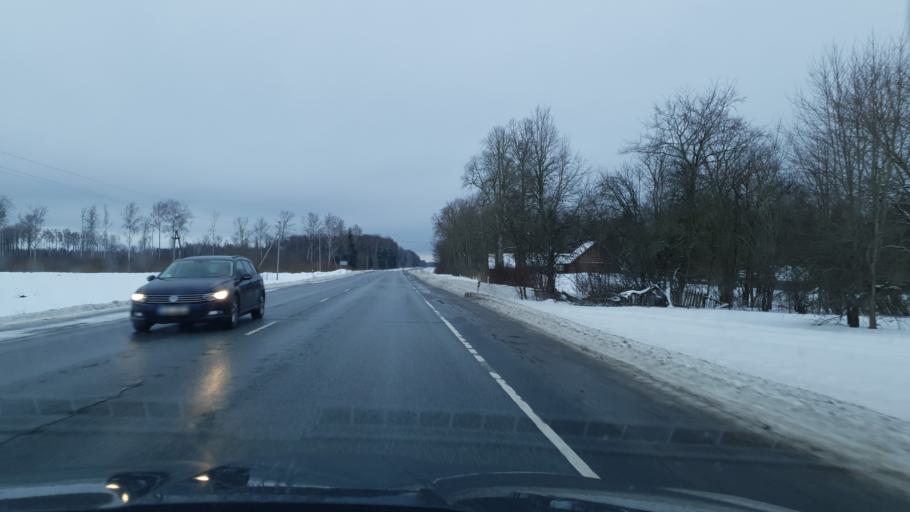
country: EE
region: Tartu
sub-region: Puhja vald
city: Puhja
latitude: 58.5486
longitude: 26.3016
